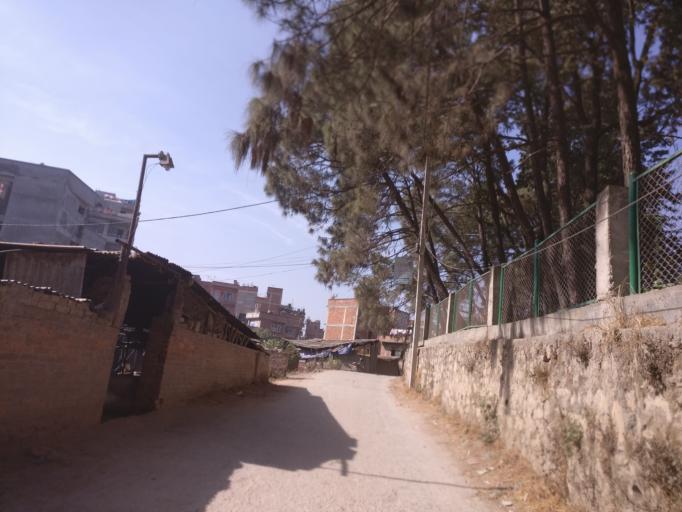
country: NP
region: Central Region
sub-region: Bagmati Zone
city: Patan
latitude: 27.6711
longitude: 85.3337
